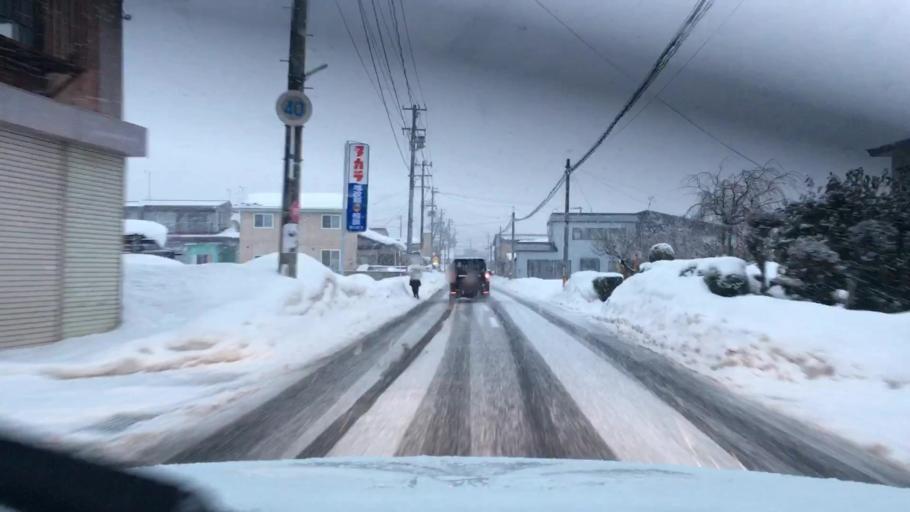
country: JP
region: Aomori
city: Hirosaki
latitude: 40.5630
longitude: 140.4867
